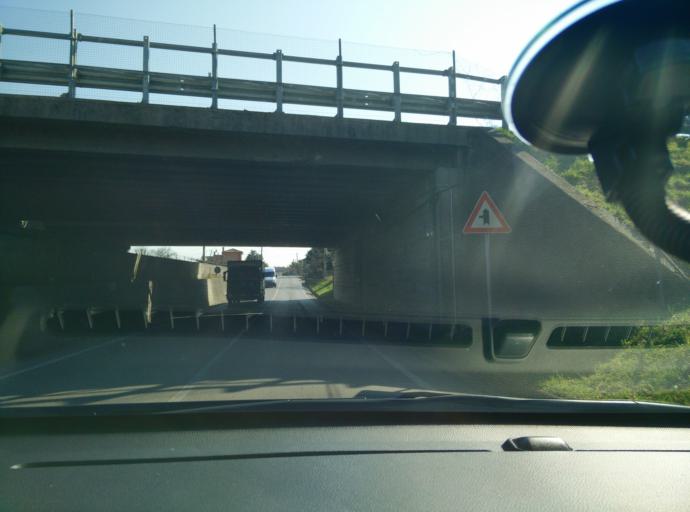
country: IT
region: Veneto
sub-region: Provincia di Treviso
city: Mareno di Piave
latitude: 45.8420
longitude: 12.3185
